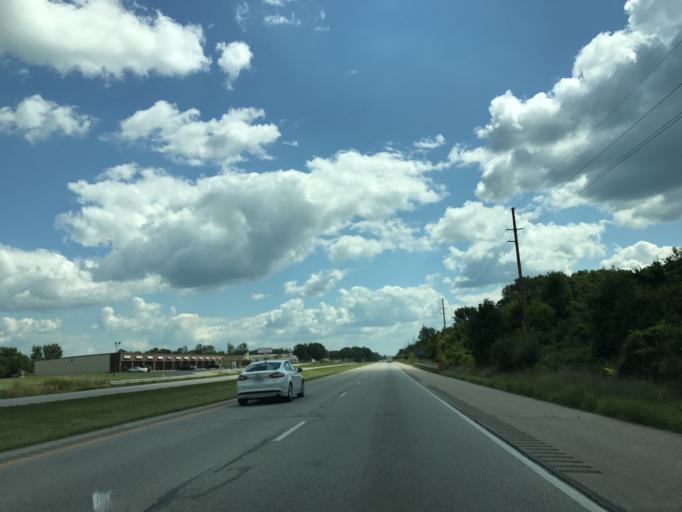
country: US
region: Indiana
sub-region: Kosciusko County
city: Winona Lake
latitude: 41.2202
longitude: -85.7771
